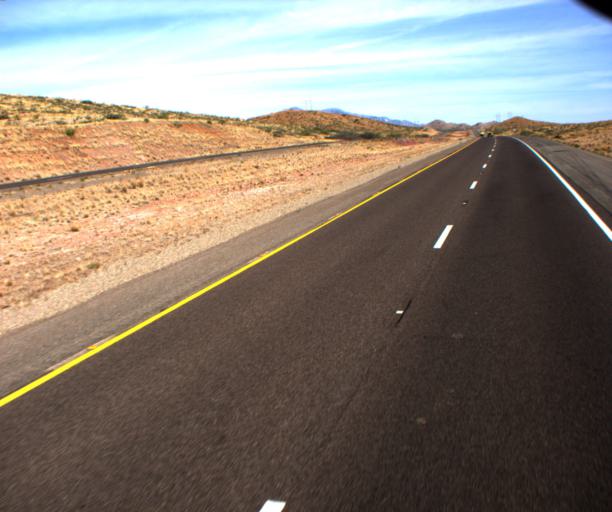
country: US
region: Arizona
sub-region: Cochise County
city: Willcox
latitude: 32.4569
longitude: -109.6654
